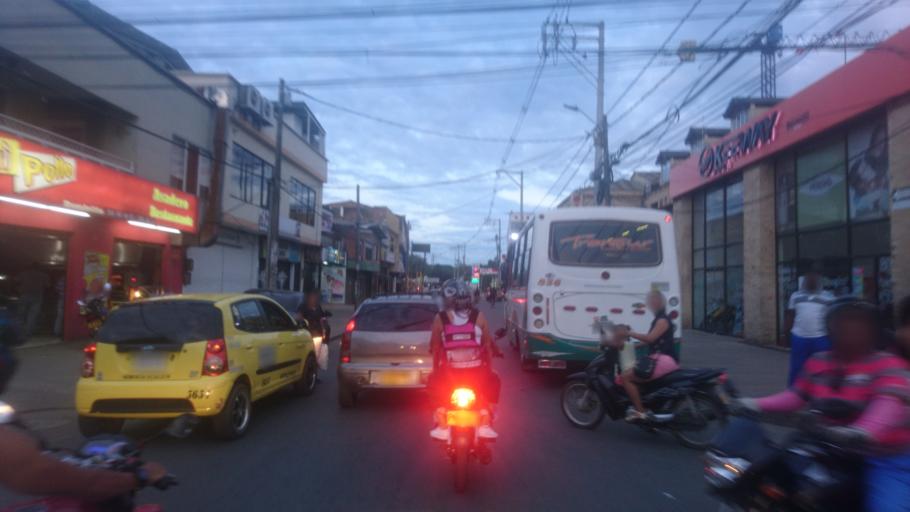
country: CO
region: Valle del Cauca
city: Jamundi
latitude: 3.2629
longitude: -76.5390
